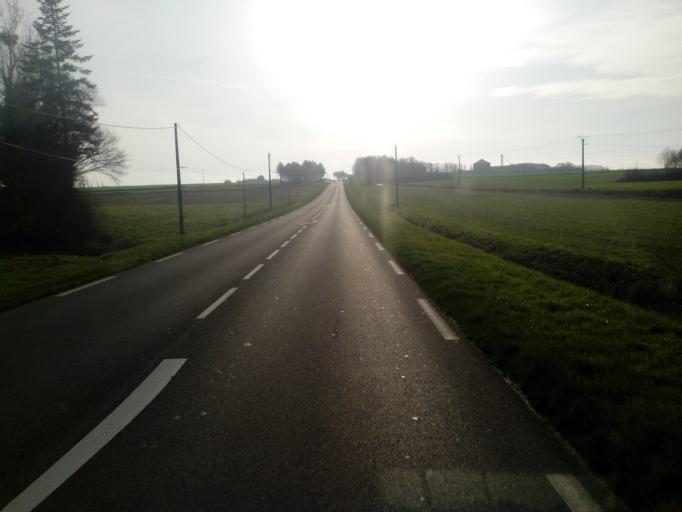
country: FR
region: Brittany
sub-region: Departement d'Ille-et-Vilaine
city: Gael
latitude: 48.1501
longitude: -2.2153
